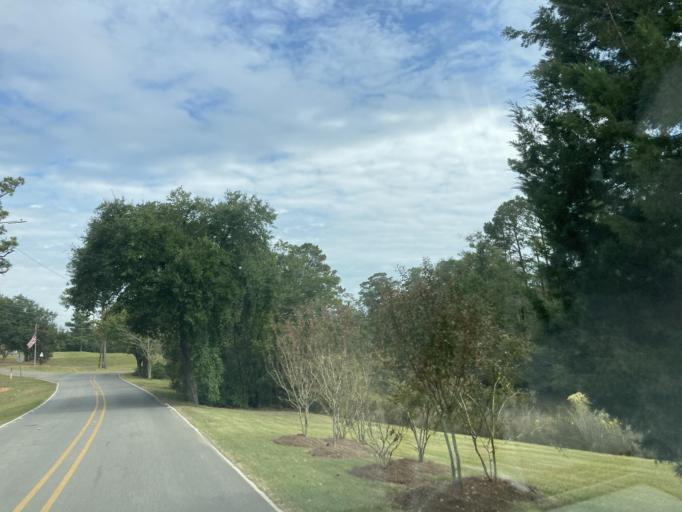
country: US
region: Mississippi
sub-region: Jackson County
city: Gulf Hills
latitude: 30.4311
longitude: -88.8382
